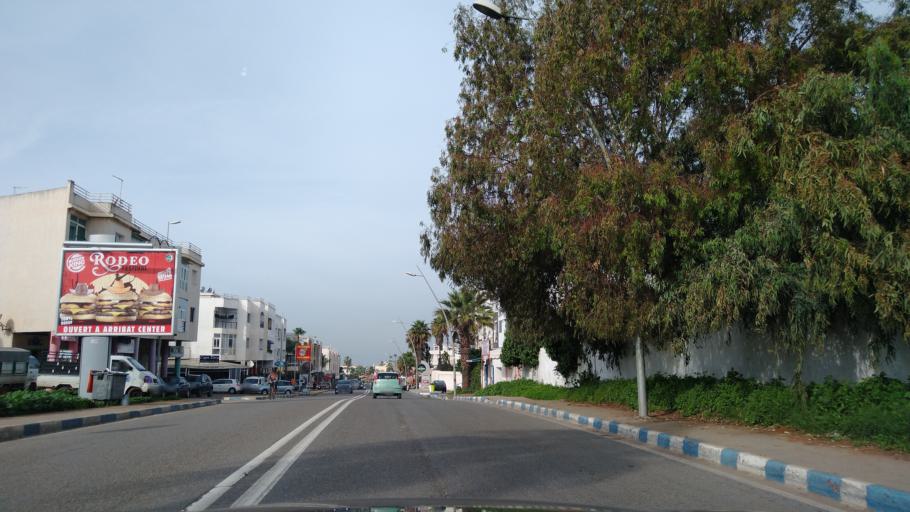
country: MA
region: Rabat-Sale-Zemmour-Zaer
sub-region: Skhirate-Temara
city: Temara
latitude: 33.9339
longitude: -6.9407
